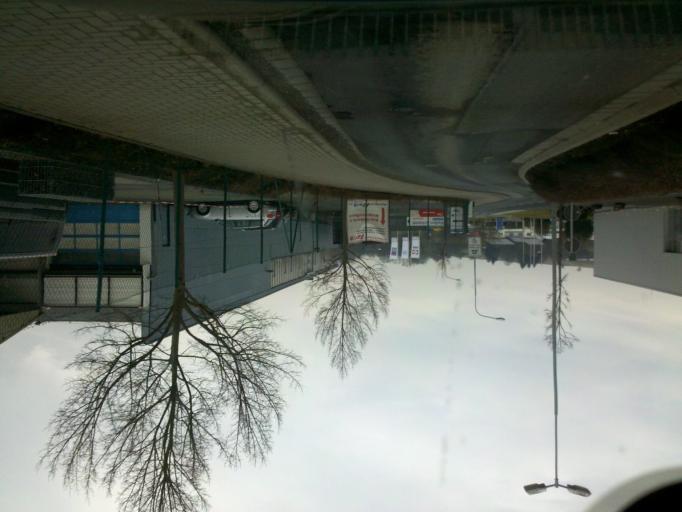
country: DE
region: Hesse
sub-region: Regierungsbezirk Giessen
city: Haiger
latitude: 50.7438
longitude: 8.2025
